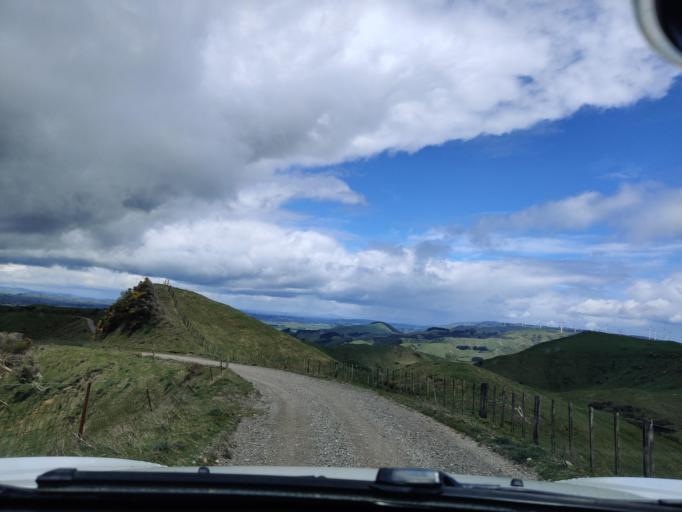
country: NZ
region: Manawatu-Wanganui
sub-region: Palmerston North City
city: Palmerston North
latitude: -40.2790
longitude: 175.8568
